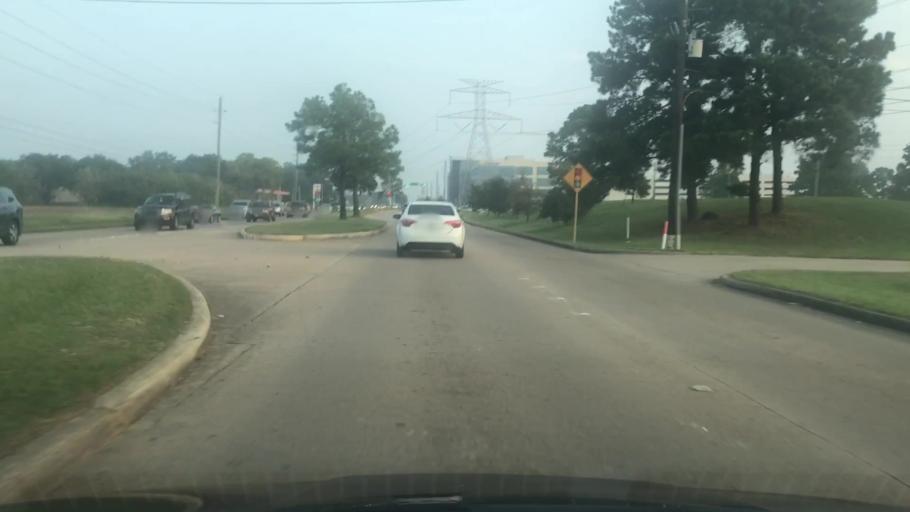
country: US
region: Texas
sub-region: Fort Bend County
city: Cinco Ranch
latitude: 29.7919
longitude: -95.7518
